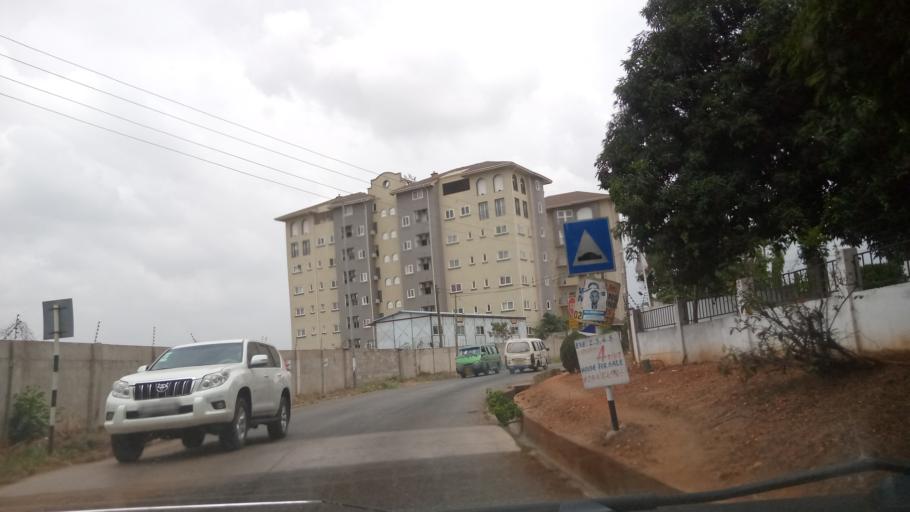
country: GH
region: Greater Accra
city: Accra
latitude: 5.6034
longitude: -0.1883
